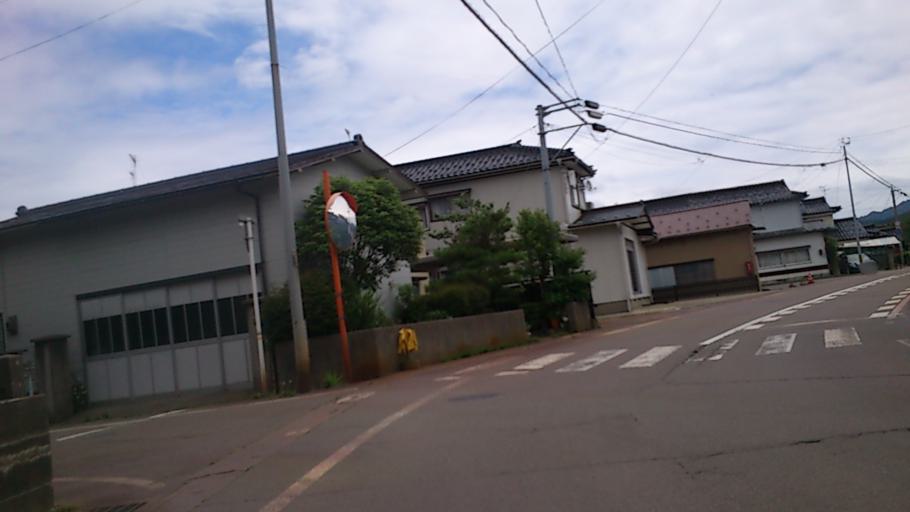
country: JP
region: Yamagata
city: Tsuruoka
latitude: 38.7918
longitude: 139.9776
